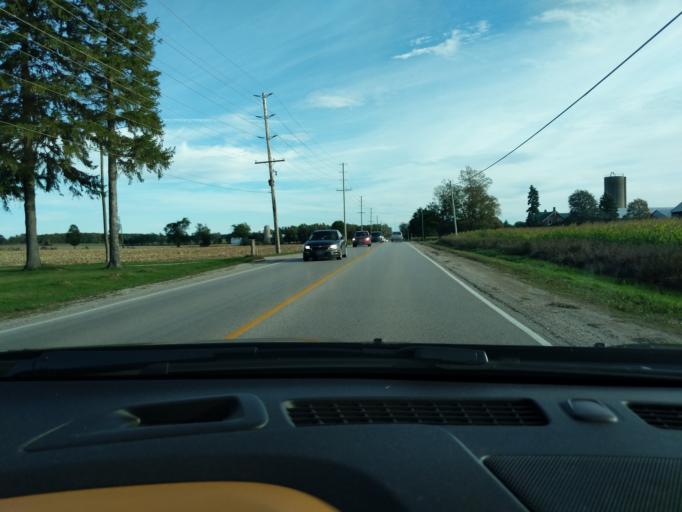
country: CA
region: Ontario
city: Barrie
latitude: 44.4084
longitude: -79.7482
